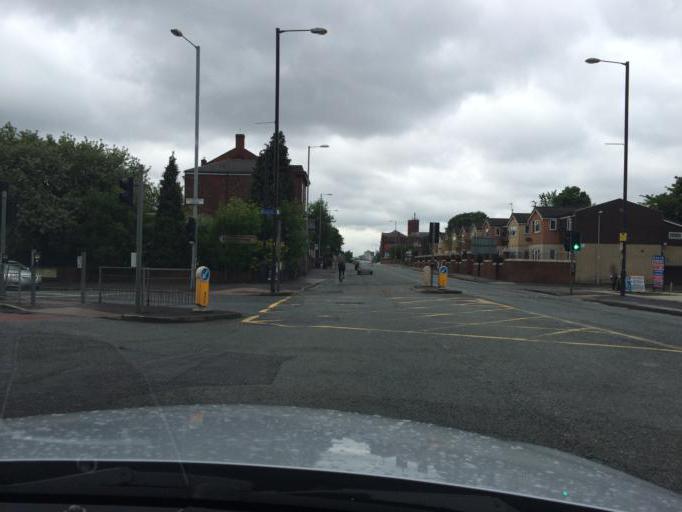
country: GB
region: England
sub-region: Manchester
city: Longsight
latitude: 53.4597
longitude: -2.2043
